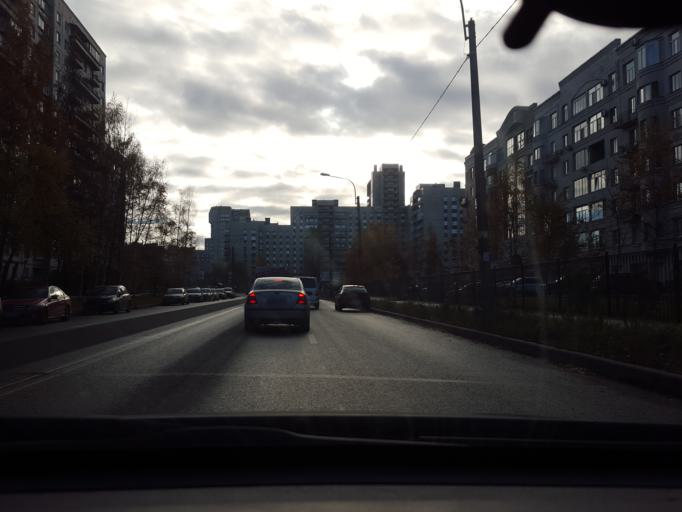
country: RU
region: St.-Petersburg
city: Ozerki
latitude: 60.0460
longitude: 30.3192
